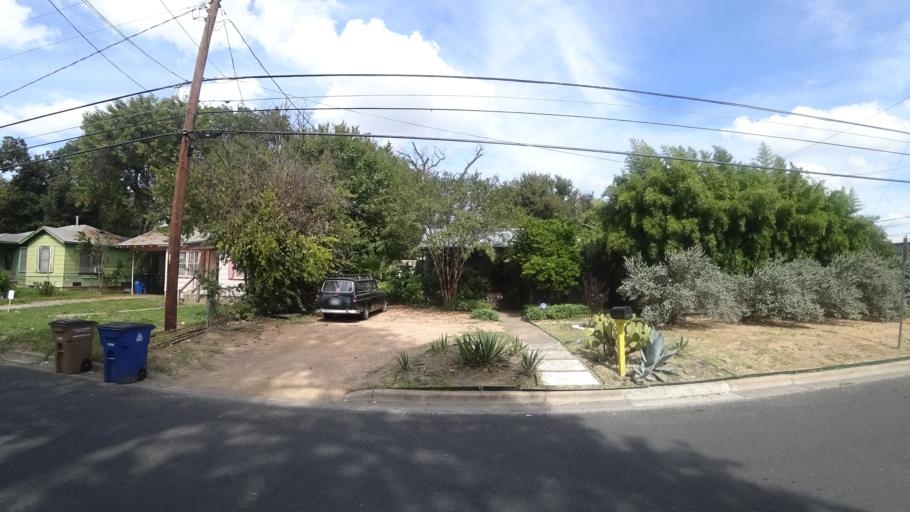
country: US
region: Texas
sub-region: Travis County
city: Austin
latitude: 30.2685
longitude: -97.6975
